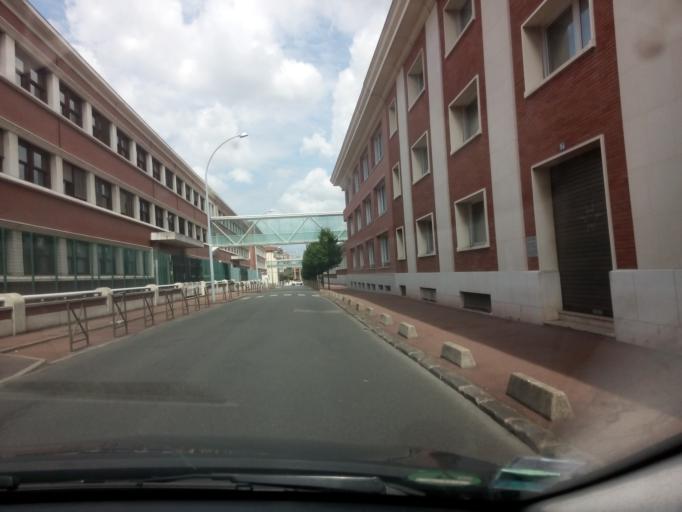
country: FR
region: Ile-de-France
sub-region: Departement des Hauts-de-Seine
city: Suresnes
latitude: 48.8578
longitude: 2.2213
